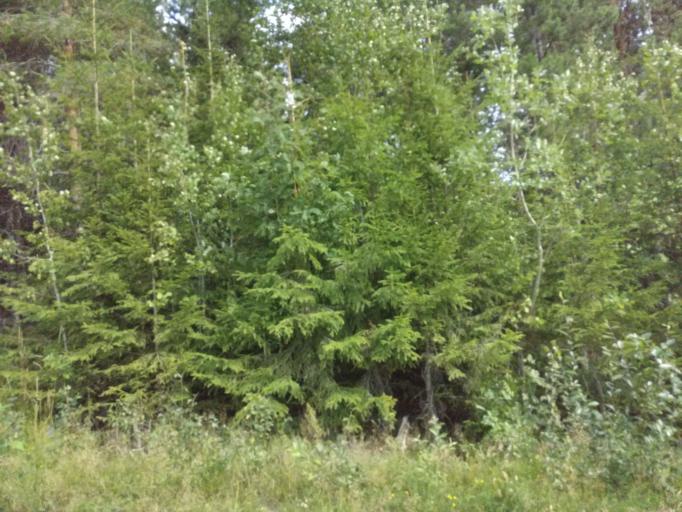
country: SE
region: Vaermland
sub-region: Hagfors Kommun
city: Hagfors
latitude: 60.0206
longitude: 13.7307
